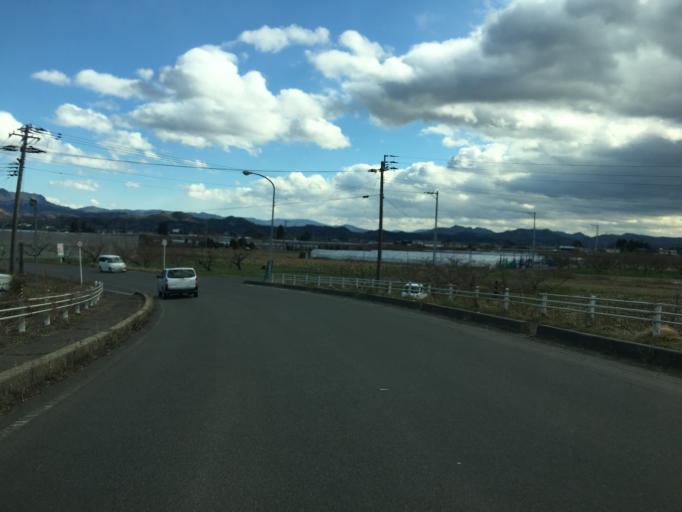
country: JP
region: Fukushima
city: Yanagawamachi-saiwaicho
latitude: 37.8601
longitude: 140.5705
